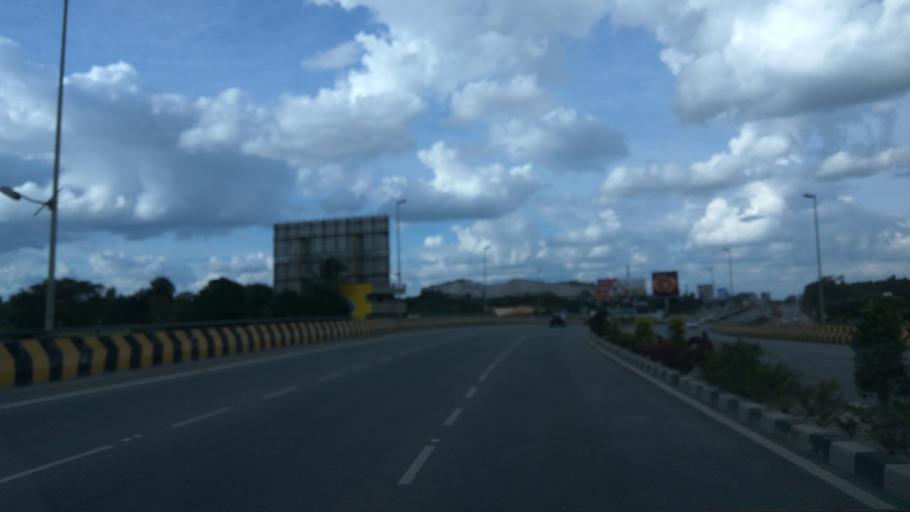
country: IN
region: Karnataka
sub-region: Bangalore Urban
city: Yelahanka
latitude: 13.1464
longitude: 77.6178
